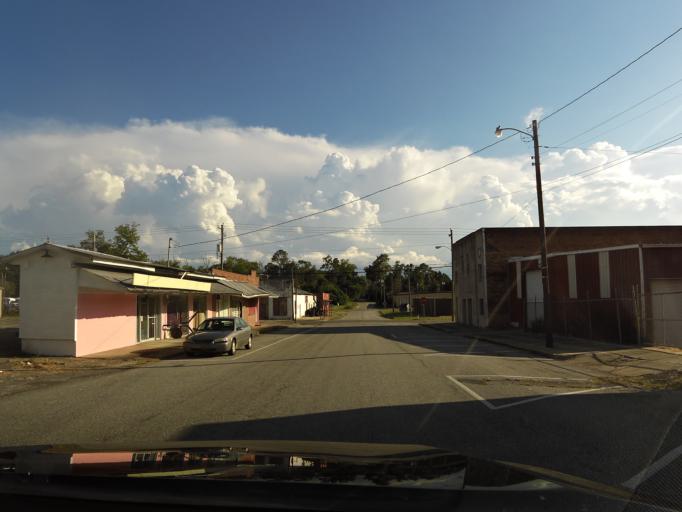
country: US
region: Georgia
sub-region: Brooks County
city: Quitman
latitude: 30.7839
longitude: -83.5591
